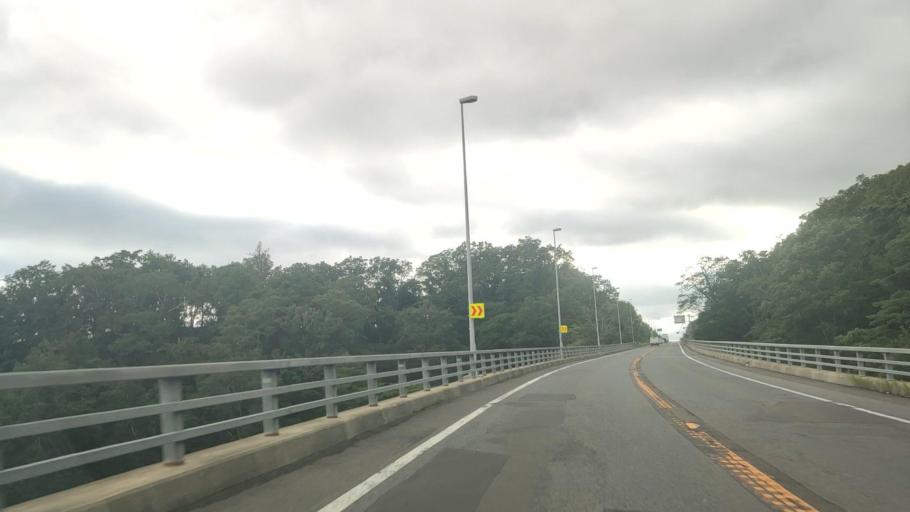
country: JP
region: Hokkaido
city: Niseko Town
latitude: 42.5934
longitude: 140.5345
